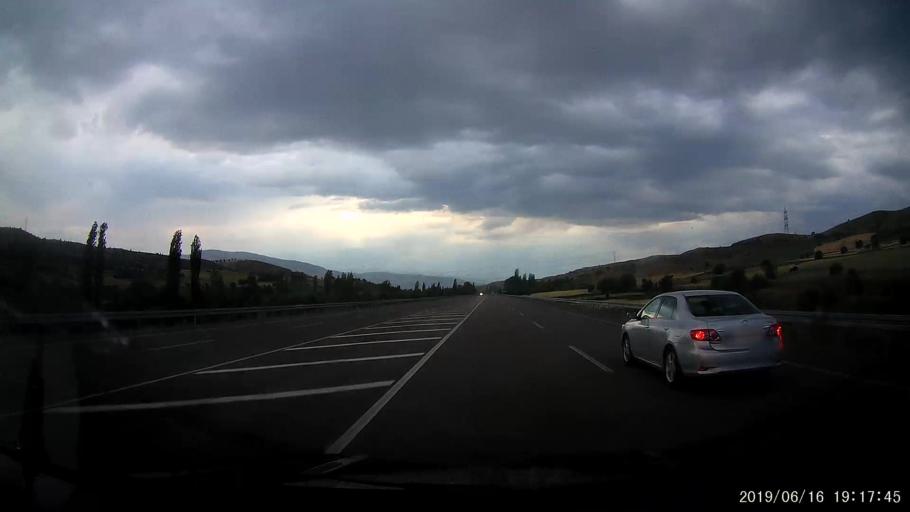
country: TR
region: Sivas
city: Akincilar
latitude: 40.0935
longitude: 38.4775
